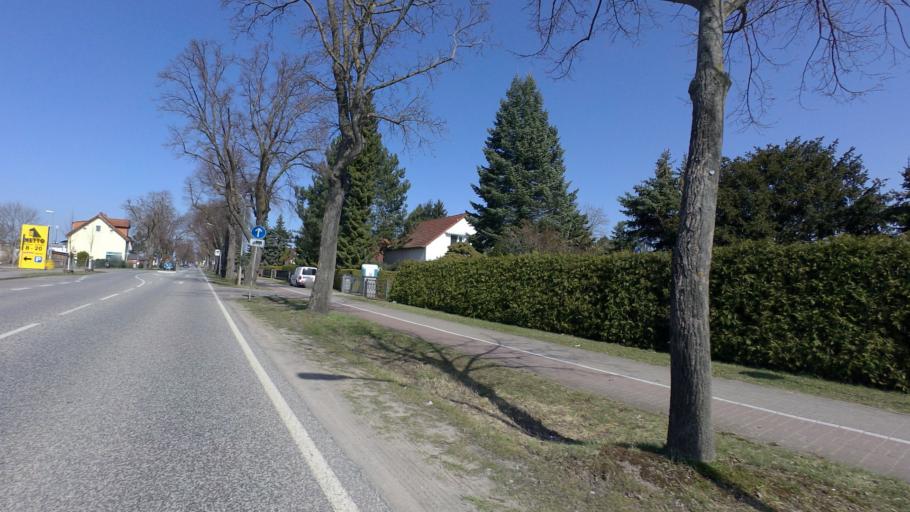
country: DE
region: Brandenburg
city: Oranienburg
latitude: 52.7281
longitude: 13.2469
